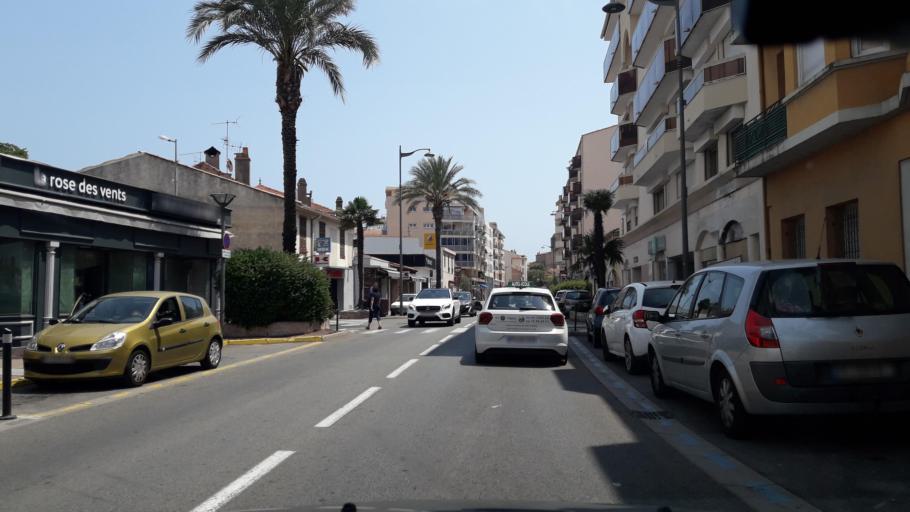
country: FR
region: Provence-Alpes-Cote d'Azur
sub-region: Departement du Var
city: Saint-Raphael
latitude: 43.4281
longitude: 6.7658
